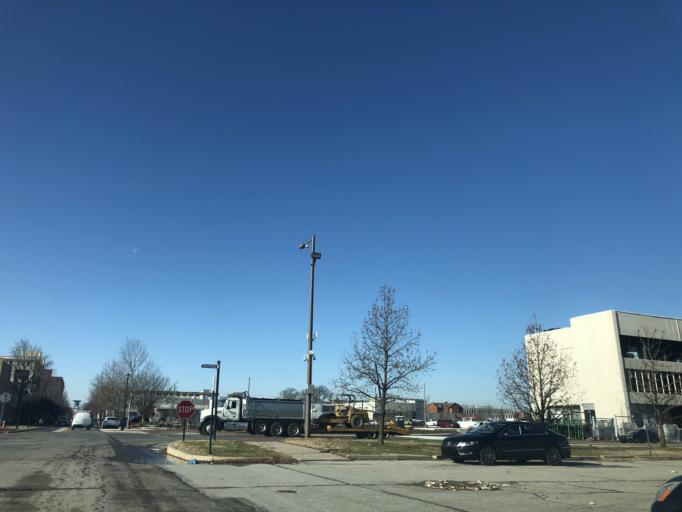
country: US
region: New Jersey
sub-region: Gloucester County
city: National Park
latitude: 39.8908
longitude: -75.1660
